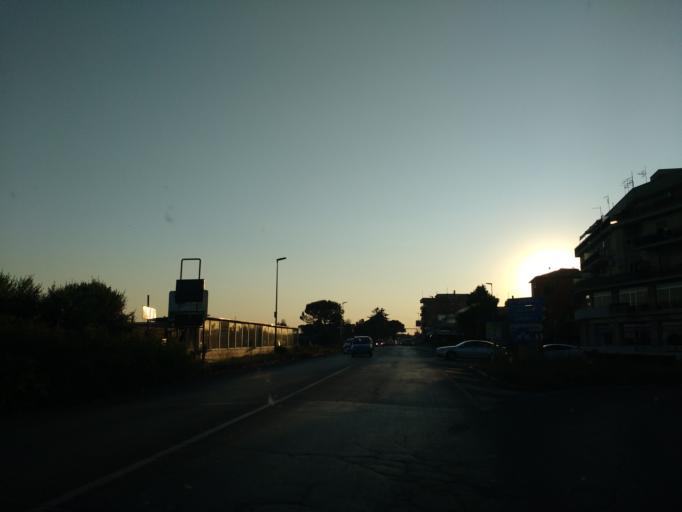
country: IT
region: Latium
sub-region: Citta metropolitana di Roma Capitale
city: Bagni di Tivoli
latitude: 41.9542
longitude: 12.7107
